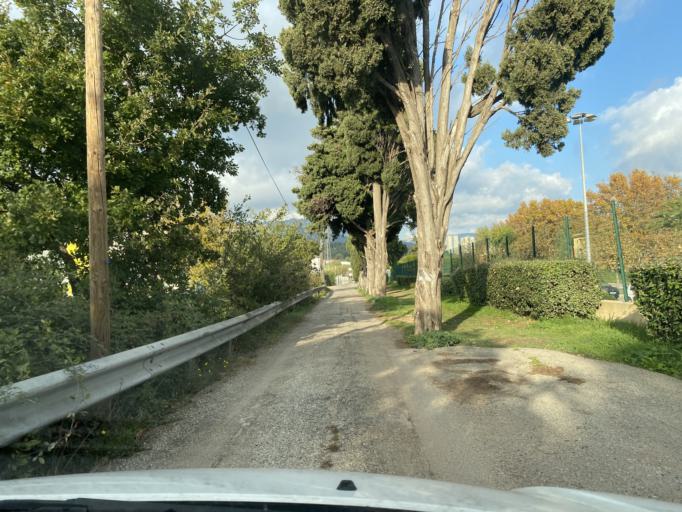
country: FR
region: Provence-Alpes-Cote d'Azur
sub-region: Departement du Var
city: La Seyne-sur-Mer
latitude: 43.1227
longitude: 5.8743
